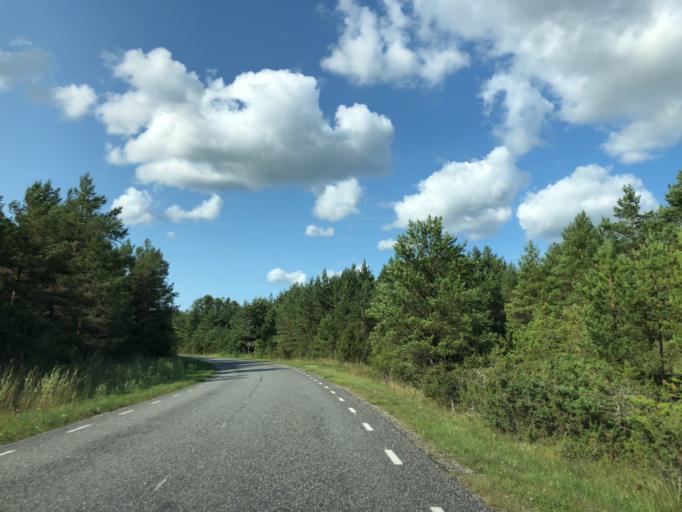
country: EE
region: Hiiumaa
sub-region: Kaerdla linn
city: Kardla
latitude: 58.8053
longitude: 22.7444
